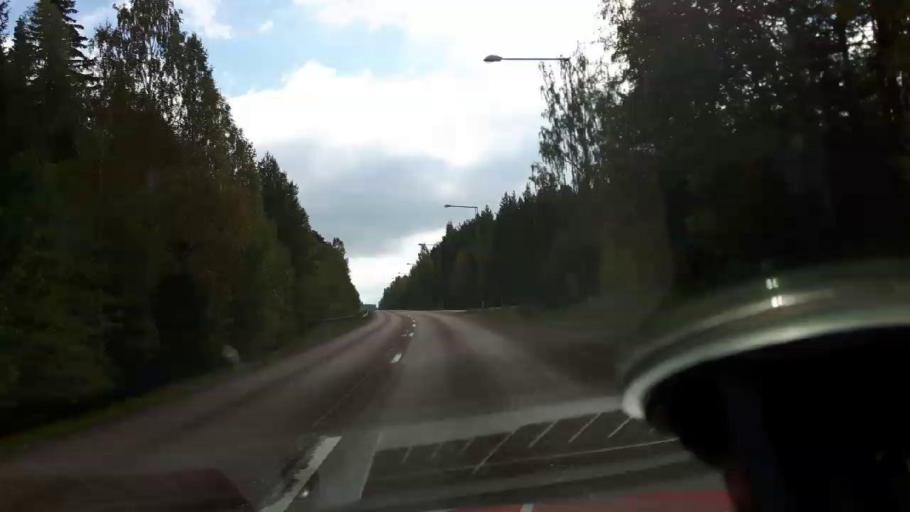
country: SE
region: Gaevleborg
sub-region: Bollnas Kommun
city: Arbra
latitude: 61.5746
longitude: 16.3187
